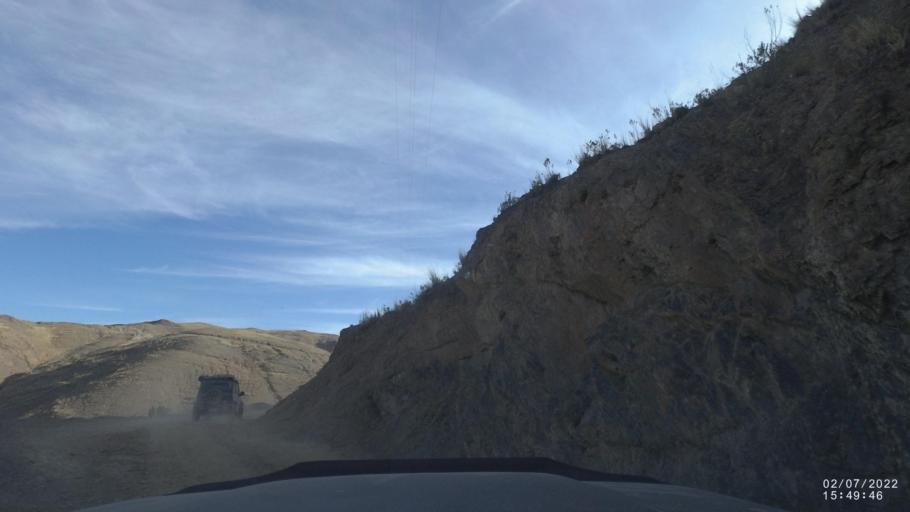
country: BO
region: Cochabamba
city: Irpa Irpa
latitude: -17.9026
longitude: -66.4112
